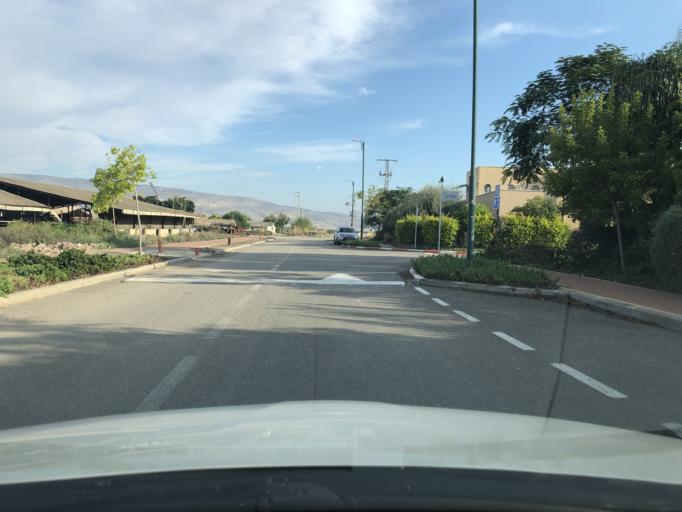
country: IL
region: Northern District
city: Yavne'el
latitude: 32.6563
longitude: 35.5781
